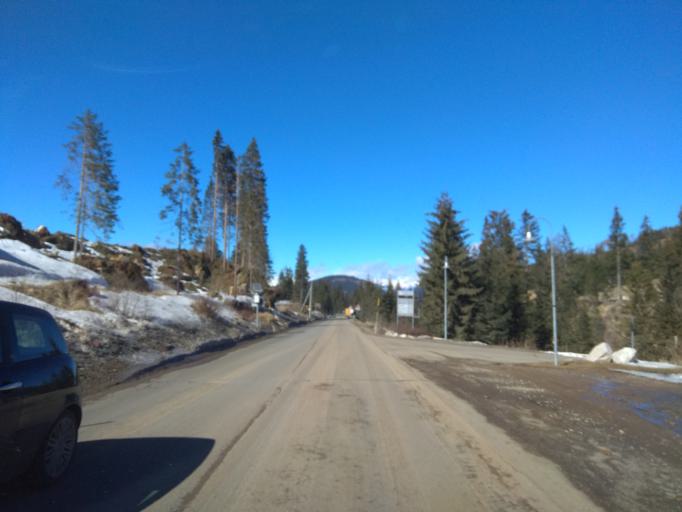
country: IT
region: Trentino-Alto Adige
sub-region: Bolzano
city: Nova Levante
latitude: 46.4102
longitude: 11.5806
